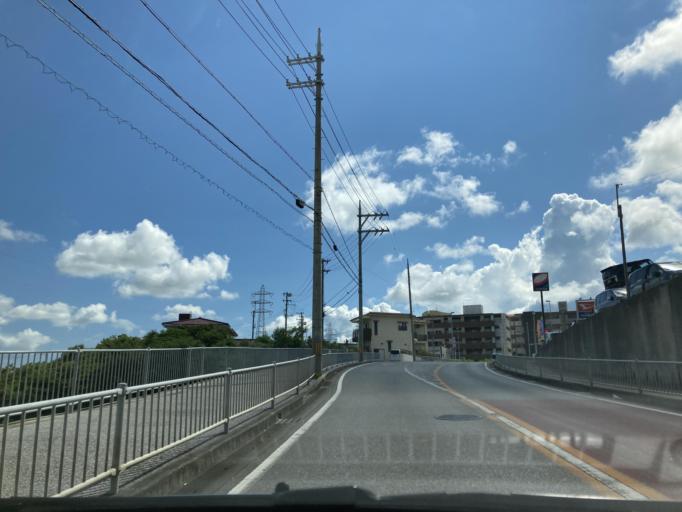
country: JP
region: Okinawa
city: Tomigusuku
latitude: 26.1643
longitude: 127.7233
